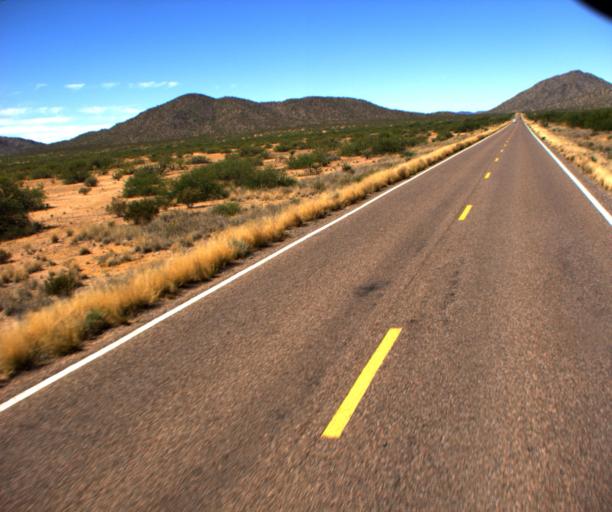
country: US
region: Arizona
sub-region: Yavapai County
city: Congress
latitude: 34.1163
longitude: -112.9687
